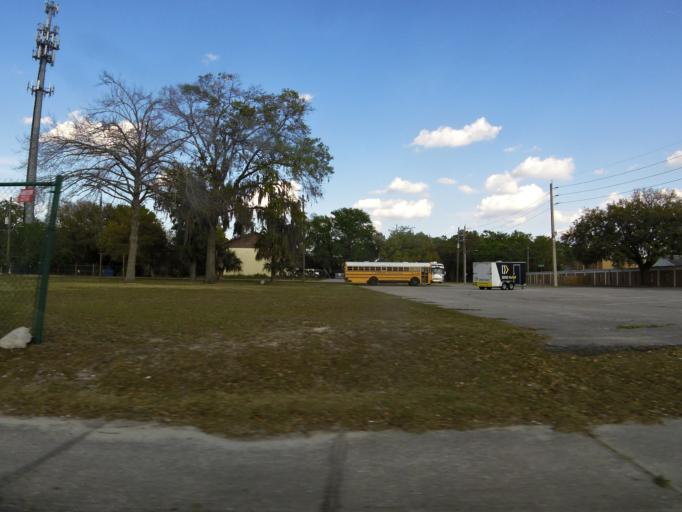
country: US
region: Florida
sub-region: Duval County
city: Jacksonville
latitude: 30.3350
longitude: -81.5969
